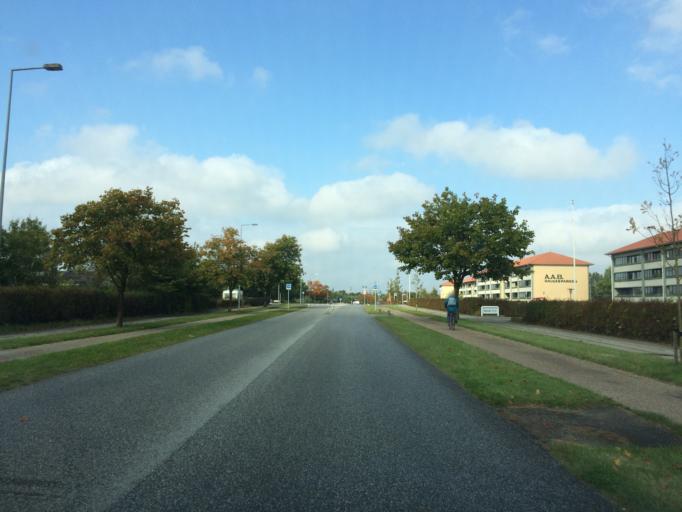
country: DK
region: Central Jutland
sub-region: Skive Kommune
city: Skive
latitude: 56.5484
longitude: 9.0185
